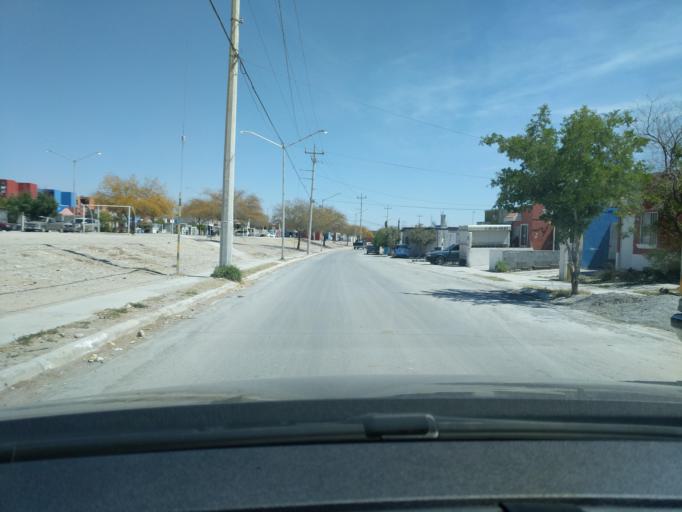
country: MX
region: Nuevo Leon
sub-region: Salinas Victoria
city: Las Torres
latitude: 25.9650
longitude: -100.3082
